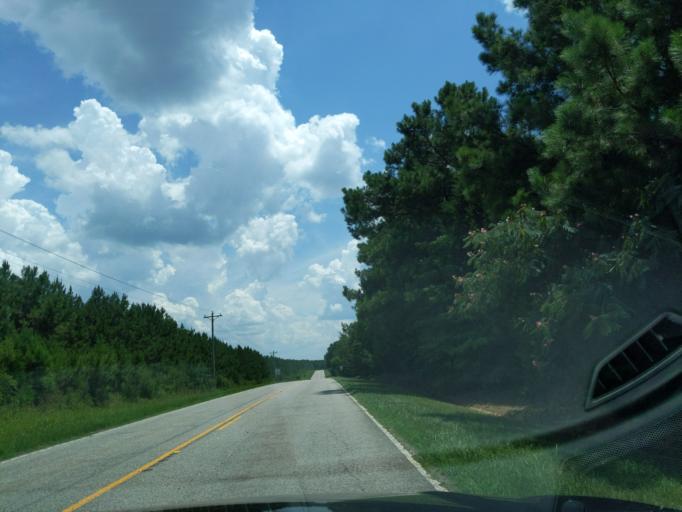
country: US
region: South Carolina
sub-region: Edgefield County
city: Edgefield
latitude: 33.9227
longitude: -82.0432
